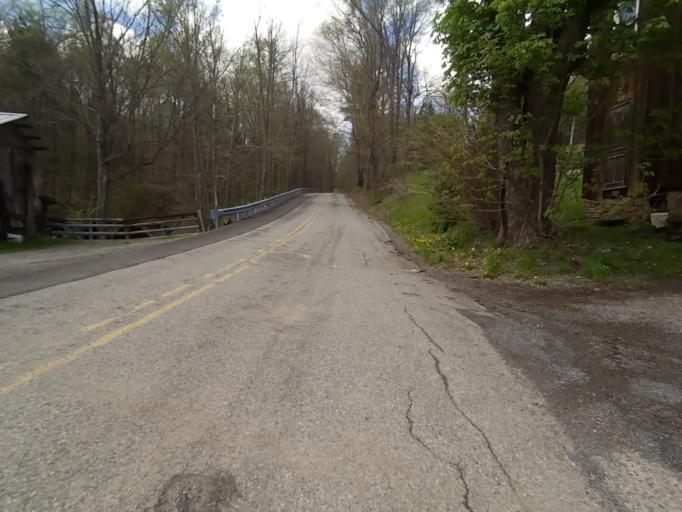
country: US
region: Pennsylvania
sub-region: Centre County
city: Milesburg
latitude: 40.9587
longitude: -77.8906
